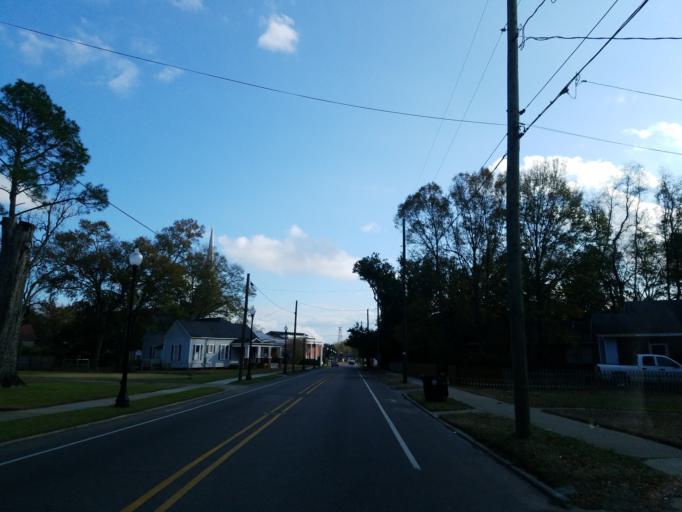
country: US
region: Mississippi
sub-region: Forrest County
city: Hattiesburg
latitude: 31.3352
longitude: -89.2988
